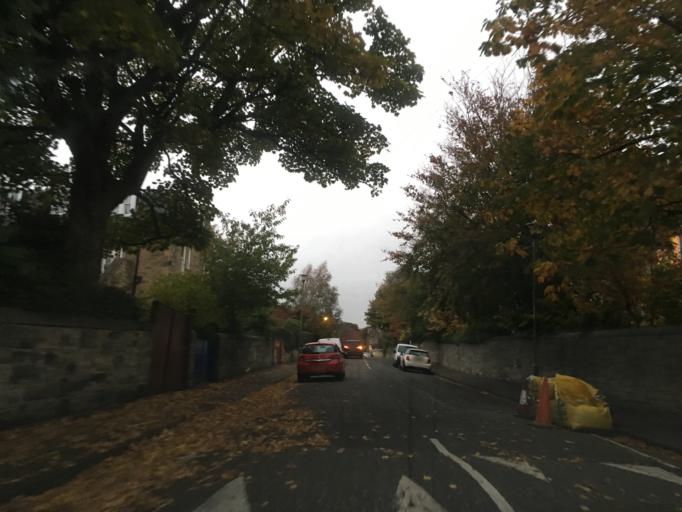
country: GB
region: Scotland
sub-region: Edinburgh
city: Edinburgh
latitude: 55.9299
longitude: -3.1854
